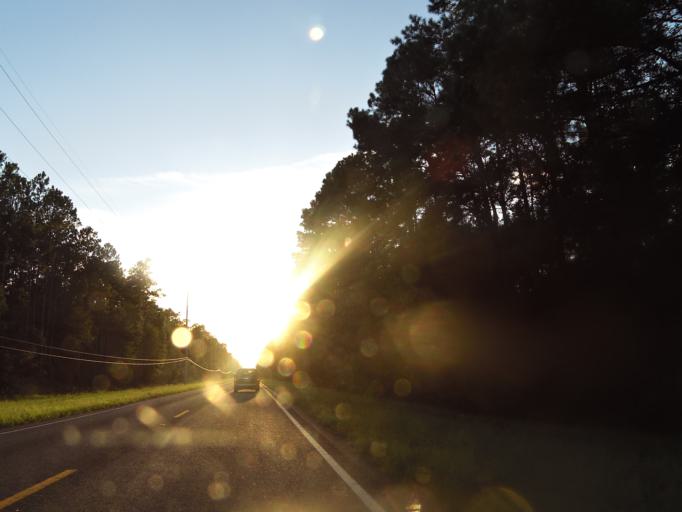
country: US
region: Georgia
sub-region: Glynn County
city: Brunswick
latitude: 31.1060
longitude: -81.6347
